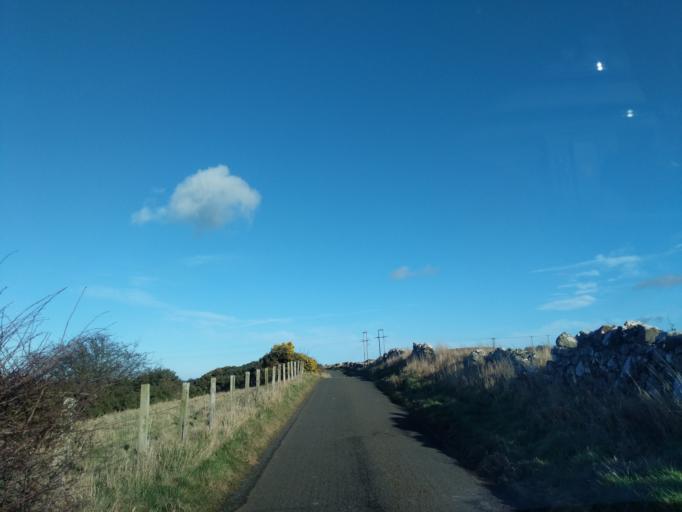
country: GB
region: Scotland
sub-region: East Lothian
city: East Linton
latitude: 55.9794
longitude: -2.6607
